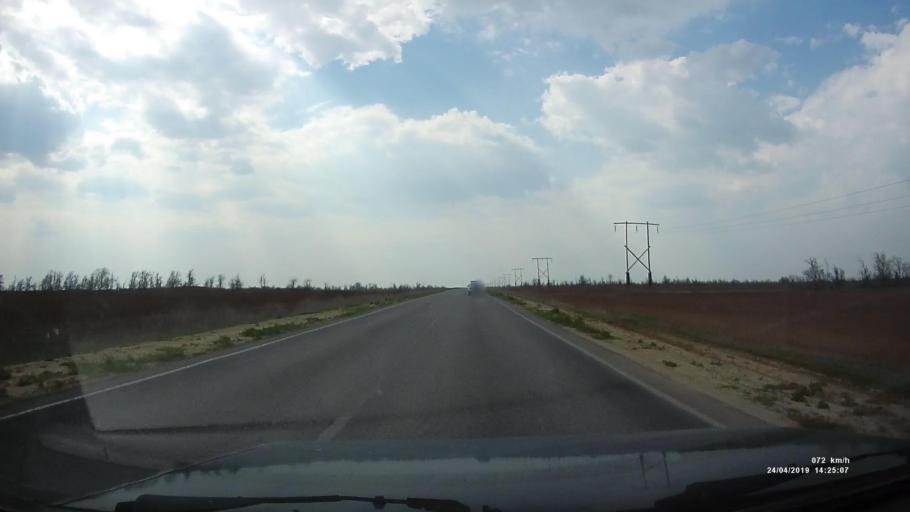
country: RU
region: Kalmykiya
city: Arshan'
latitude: 46.3300
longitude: 44.0851
